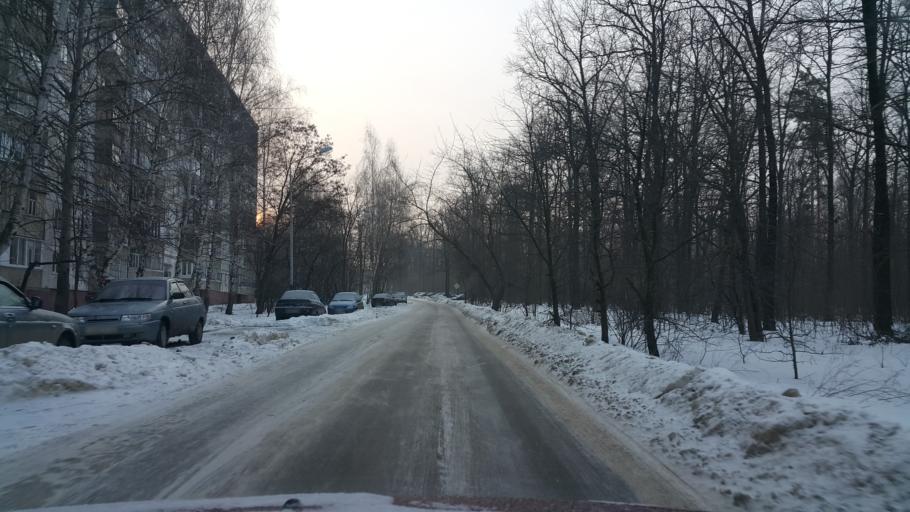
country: RU
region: Tambov
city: Kotovsk
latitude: 52.5750
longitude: 41.5171
